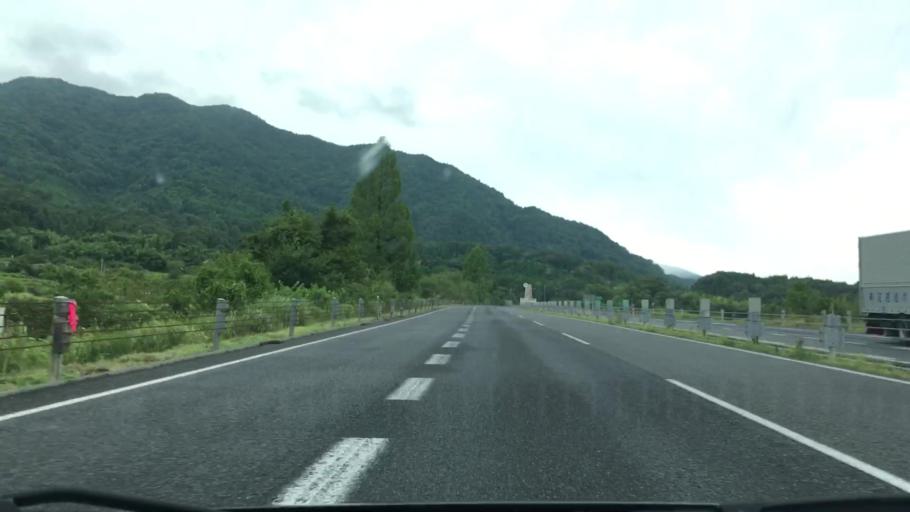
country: JP
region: Hiroshima
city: Hiroshima-shi
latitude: 34.6363
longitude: 132.5142
